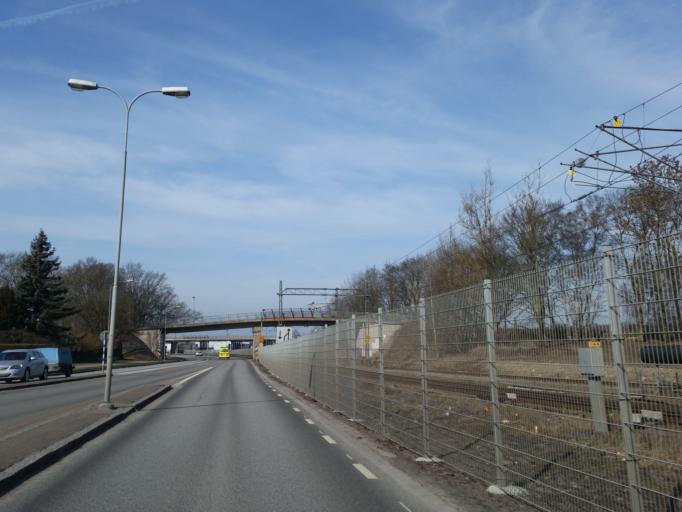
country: SE
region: Kalmar
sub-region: Kalmar Kommun
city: Kalmar
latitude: 56.6691
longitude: 16.3220
